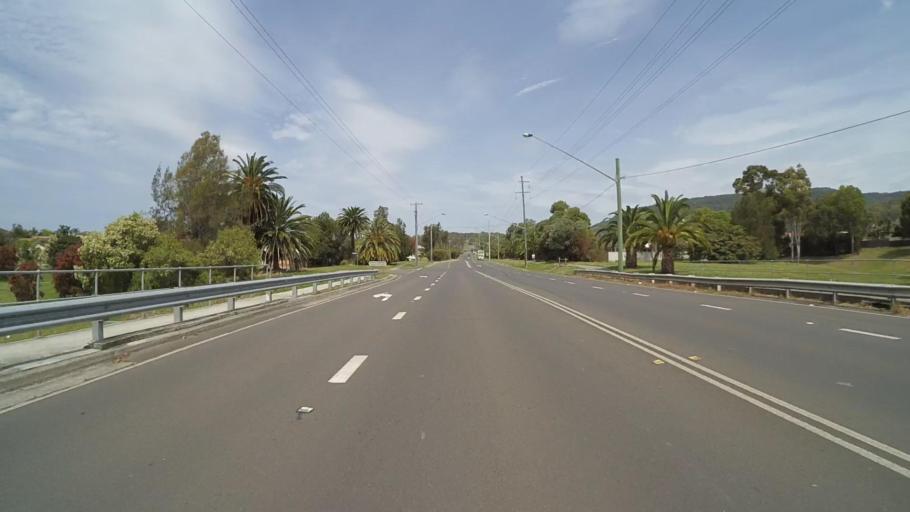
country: AU
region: New South Wales
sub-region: Shellharbour
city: Albion Park Rail
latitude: -34.5852
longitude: 150.7792
